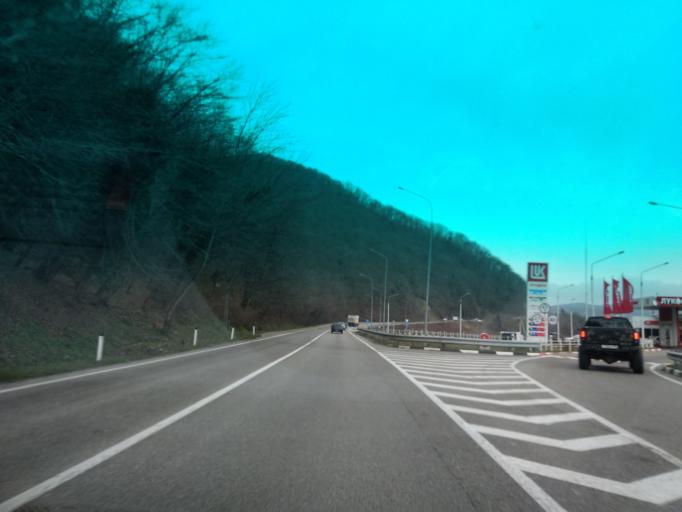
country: RU
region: Krasnodarskiy
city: Ol'ginka
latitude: 44.2166
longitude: 38.8946
